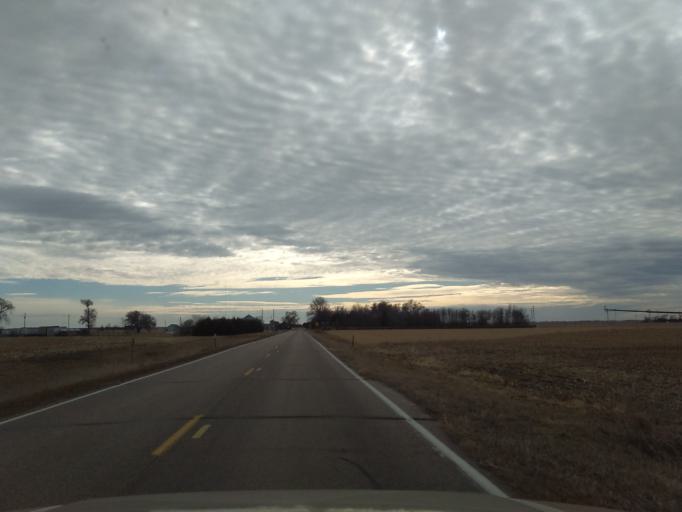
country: US
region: Nebraska
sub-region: Buffalo County
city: Gibbon
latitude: 40.6508
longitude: -98.8473
